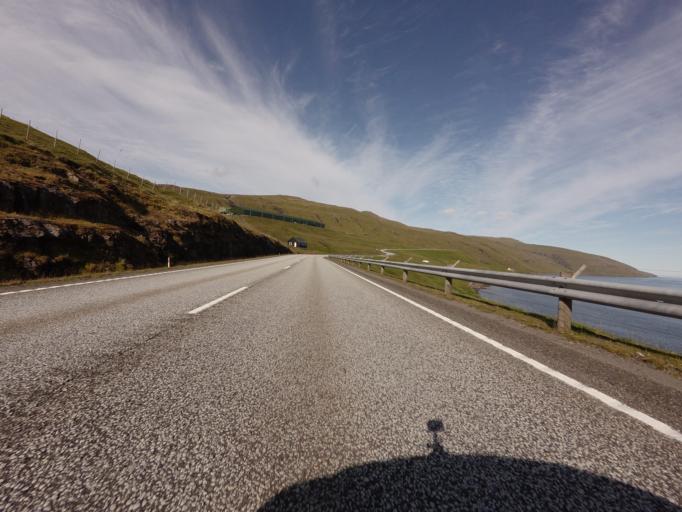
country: FO
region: Streymoy
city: Vestmanna
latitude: 62.1003
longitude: -7.1314
